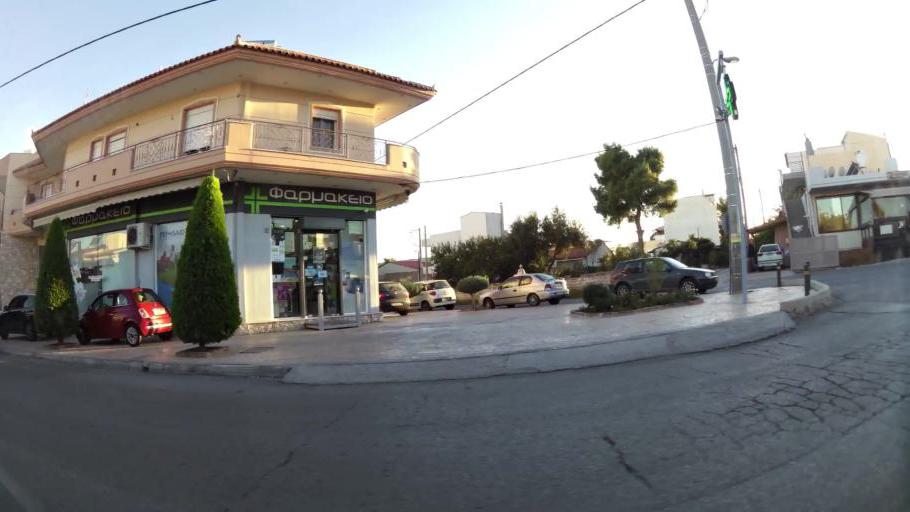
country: GR
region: Attica
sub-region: Nomarchia Dytikis Attikis
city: Ano Liosia
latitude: 38.0889
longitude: 23.7005
